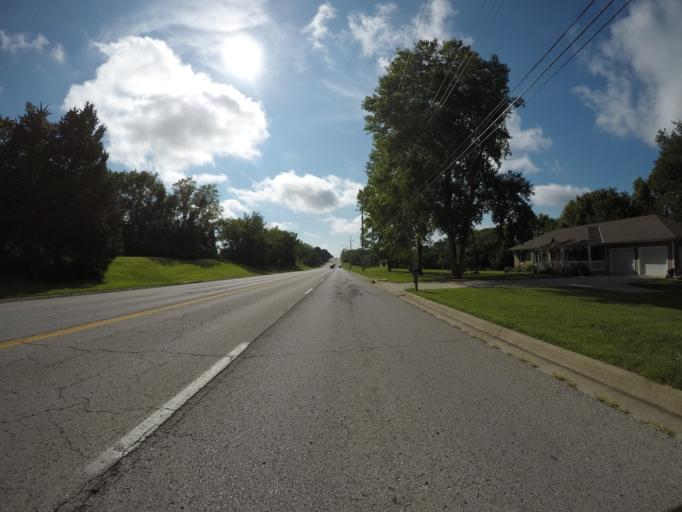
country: US
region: Kansas
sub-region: Leavenworth County
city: Basehor
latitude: 39.1287
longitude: -94.8856
